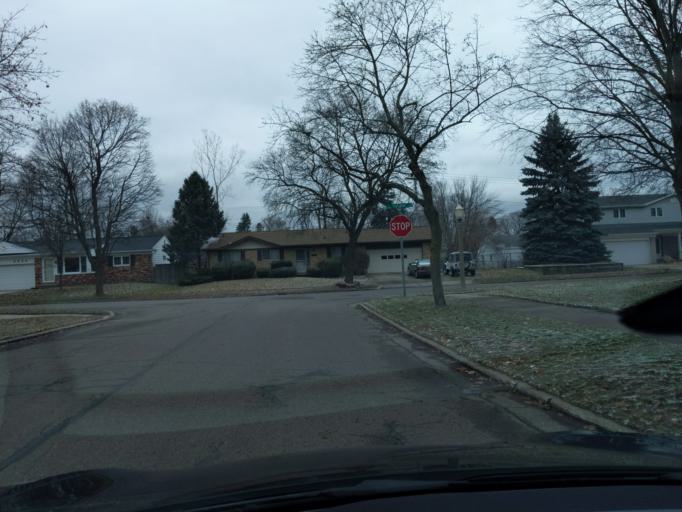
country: US
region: Michigan
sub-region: Ingham County
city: East Lansing
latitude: 42.7555
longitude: -84.5120
